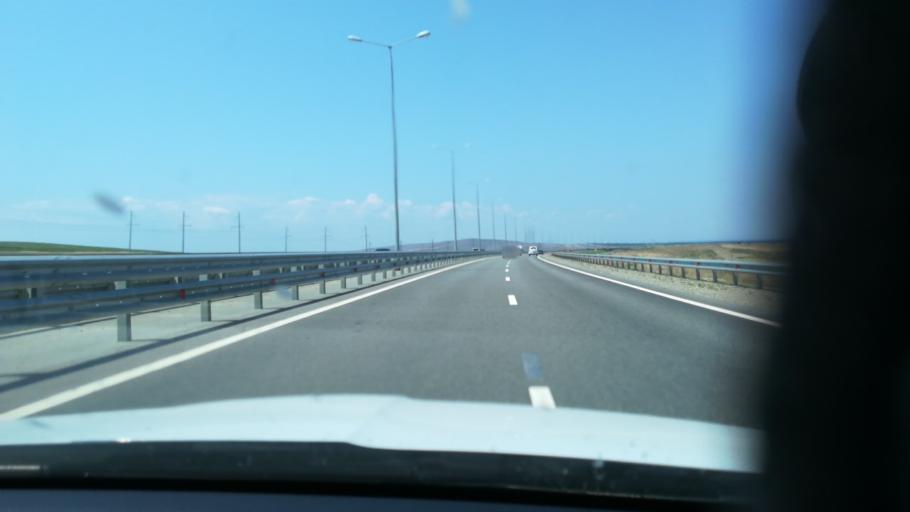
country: RU
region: Krasnodarskiy
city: Vyshestebliyevskaya
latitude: 45.2277
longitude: 36.9717
